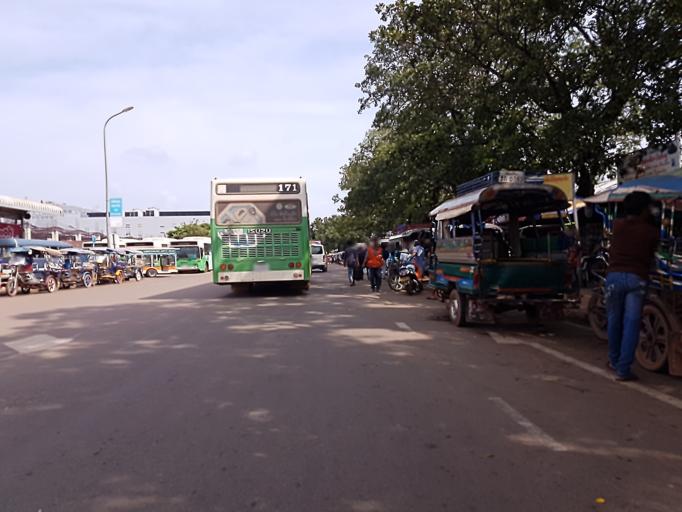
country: LA
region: Vientiane
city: Vientiane
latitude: 17.9636
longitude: 102.6150
